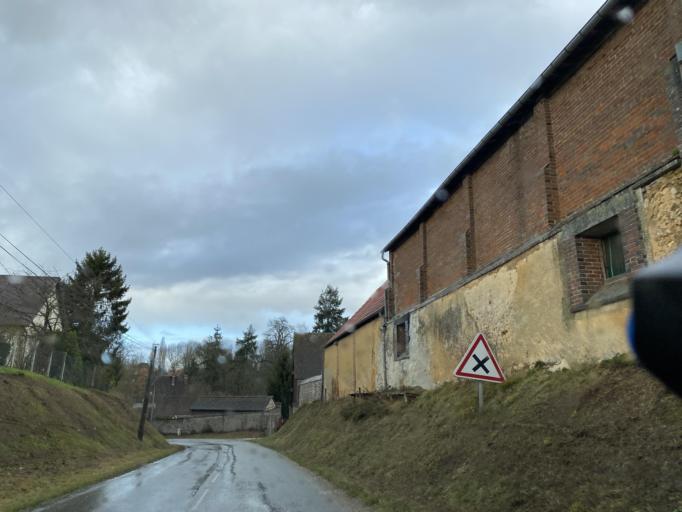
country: FR
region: Haute-Normandie
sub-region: Departement de l'Eure
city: Tillieres-sur-Avre
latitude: 48.7559
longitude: 1.0616
